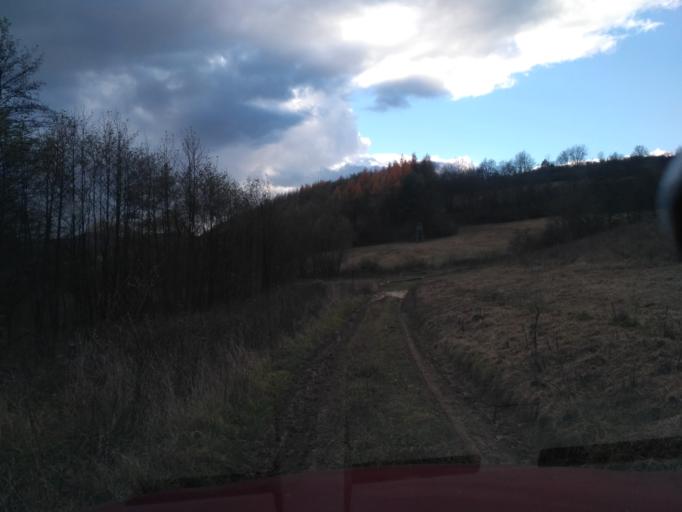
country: SK
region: Presovsky
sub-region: Okres Presov
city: Presov
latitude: 48.9301
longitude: 21.2077
